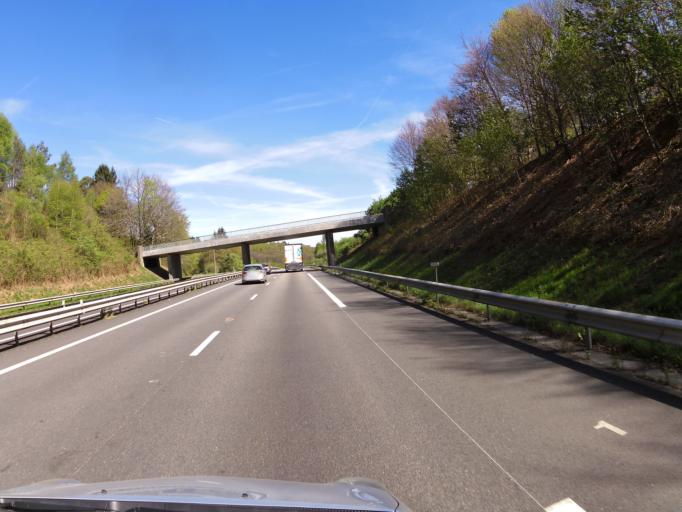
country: FR
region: Limousin
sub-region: Departement de la Haute-Vienne
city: Razes
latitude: 46.0035
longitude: 1.3381
